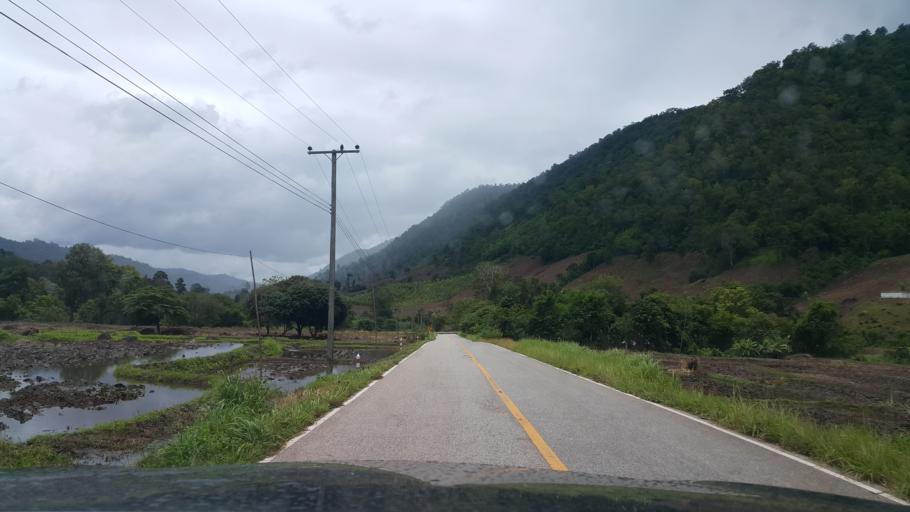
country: TH
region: Loei
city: Na Haeo
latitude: 17.5488
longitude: 100.8413
